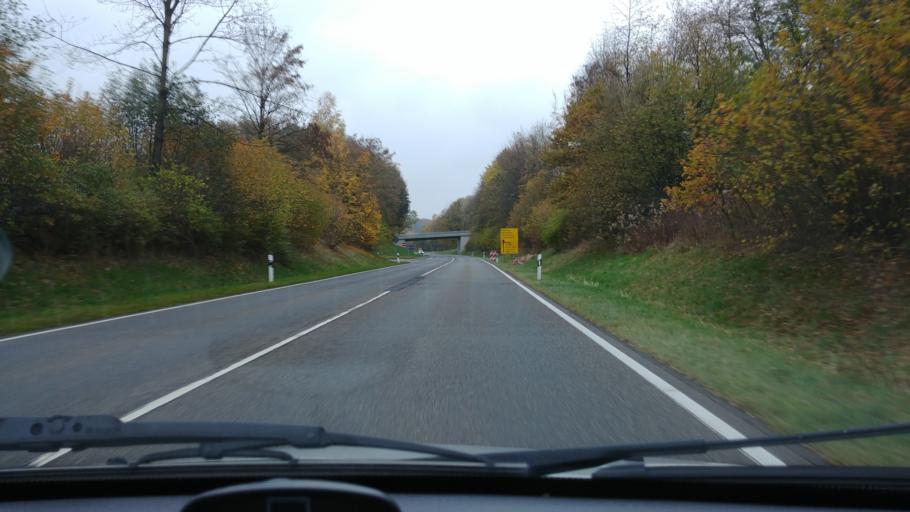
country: DE
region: Rheinland-Pfalz
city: Rotenhain
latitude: 50.6037
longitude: 7.8893
